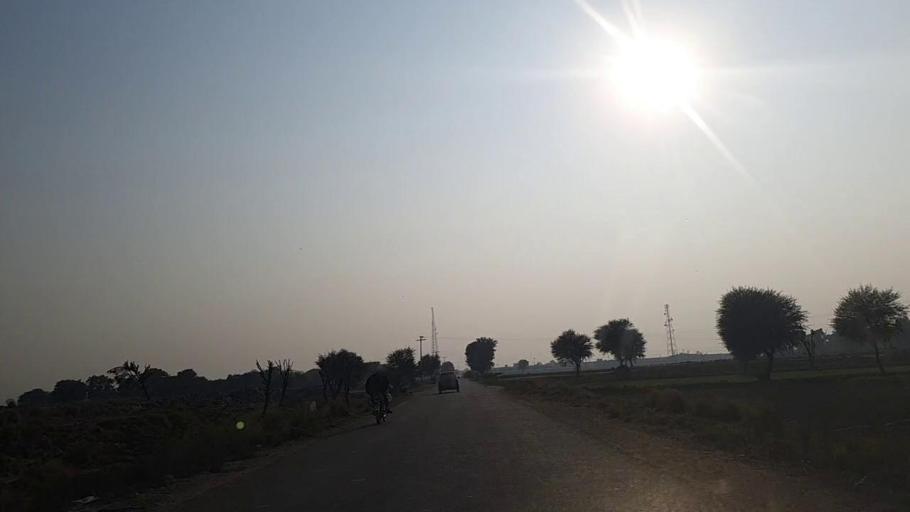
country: PK
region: Sindh
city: Shahpur Chakar
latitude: 26.2037
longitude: 68.5592
